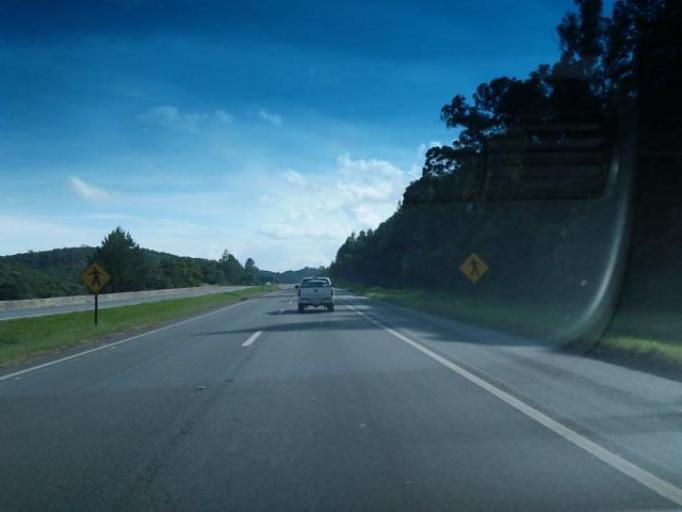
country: BR
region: Parana
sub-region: Campina Grande Do Sul
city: Campina Grande do Sul
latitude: -25.2212
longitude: -48.9054
